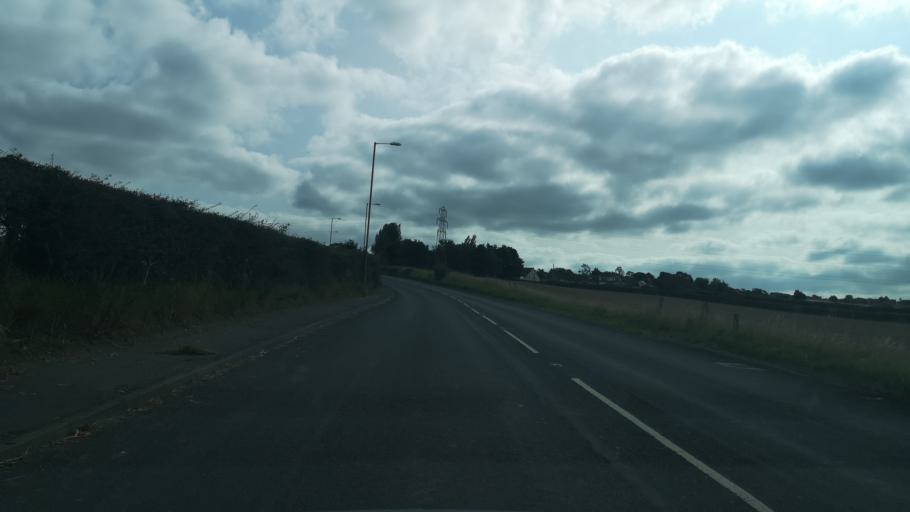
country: GB
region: England
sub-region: City and Borough of Wakefield
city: Horbury
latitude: 53.6533
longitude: -1.5747
